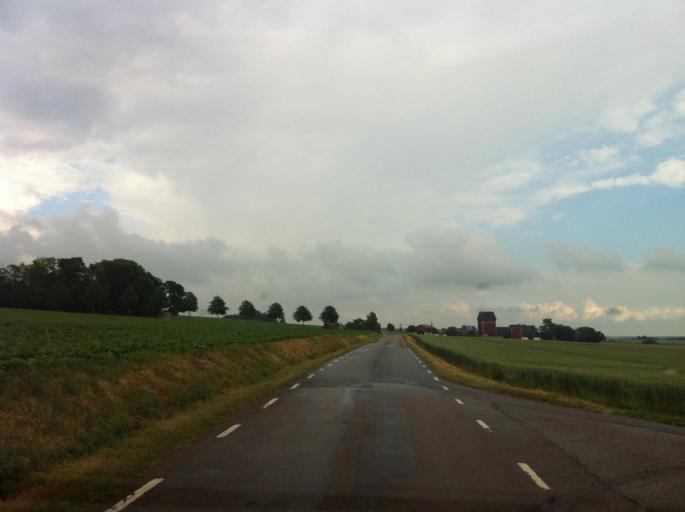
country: SE
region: Skane
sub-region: Helsingborg
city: Glumslov
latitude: 55.9249
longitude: 12.8734
